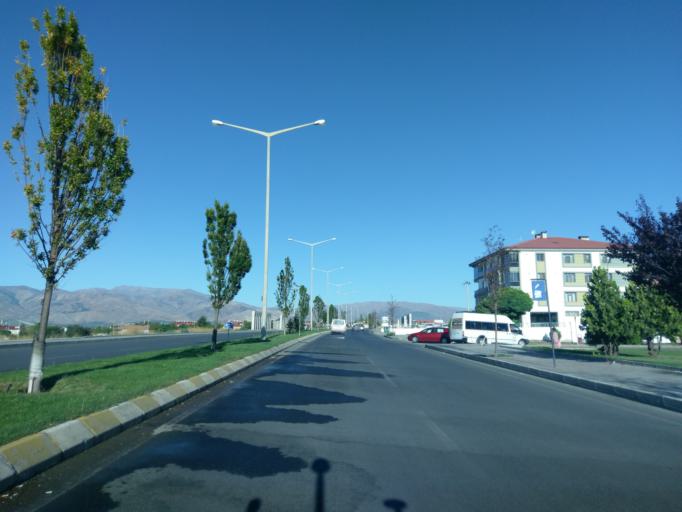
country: TR
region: Erzincan
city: Erzincan
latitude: 39.7492
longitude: 39.4625
